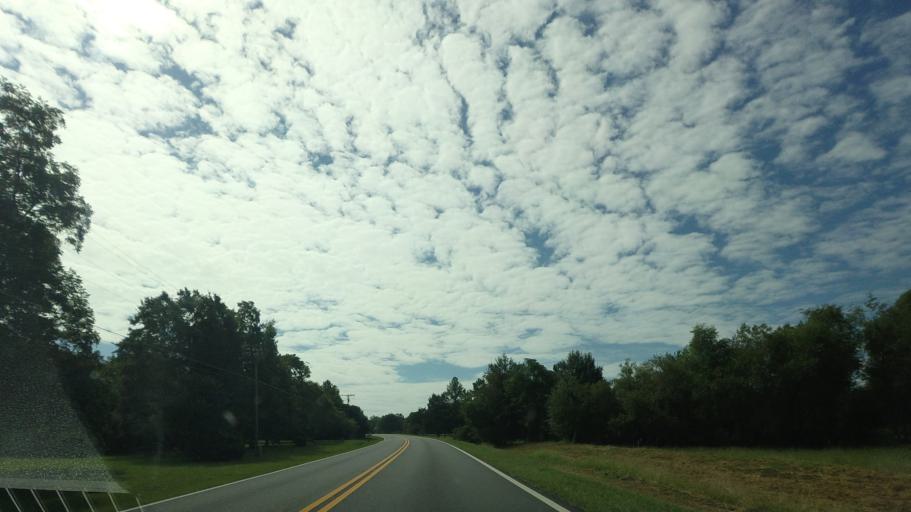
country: US
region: Georgia
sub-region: Houston County
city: Centerville
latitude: 32.6489
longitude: -83.6950
